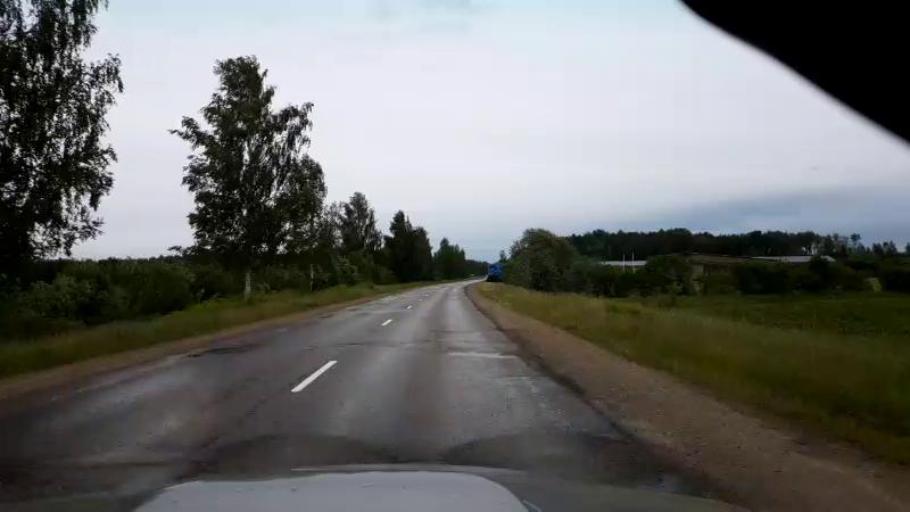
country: LV
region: Kekava
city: Kekava
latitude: 56.8098
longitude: 24.2713
